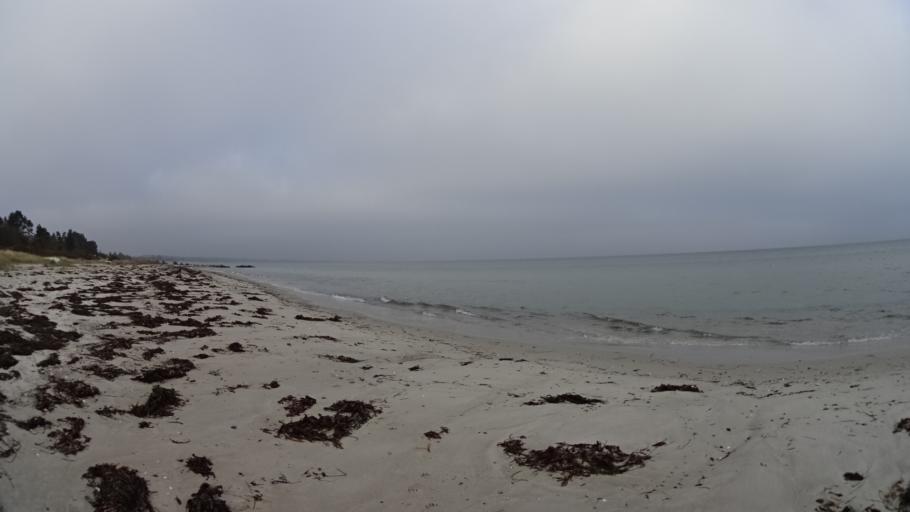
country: DK
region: Central Jutland
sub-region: Arhus Kommune
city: Malling
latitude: 55.9671
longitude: 10.2607
